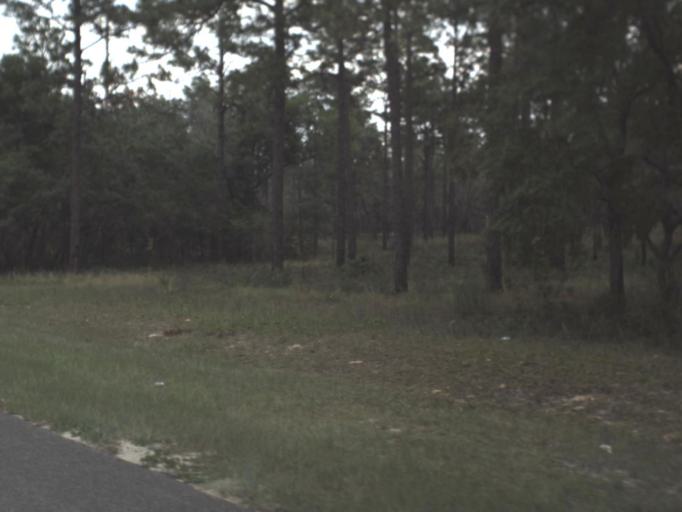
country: US
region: Florida
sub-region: Putnam County
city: Crescent City
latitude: 29.4107
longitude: -81.7370
